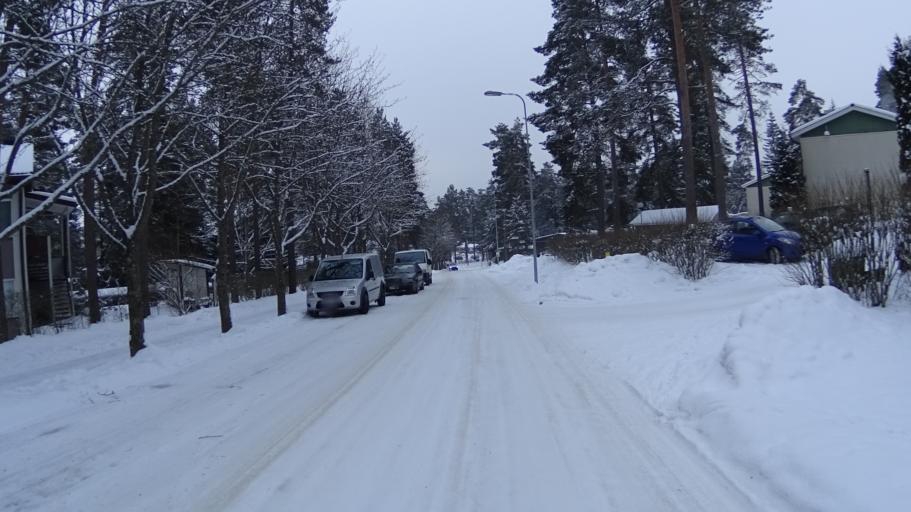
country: FI
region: Uusimaa
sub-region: Helsinki
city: Vihti
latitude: 60.3313
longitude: 24.2983
